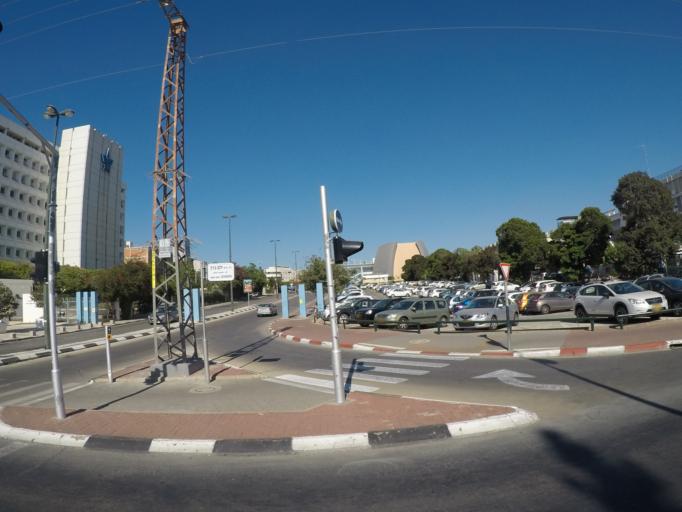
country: IL
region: Tel Aviv
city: Ramat Gan
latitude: 32.1106
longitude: 34.8017
